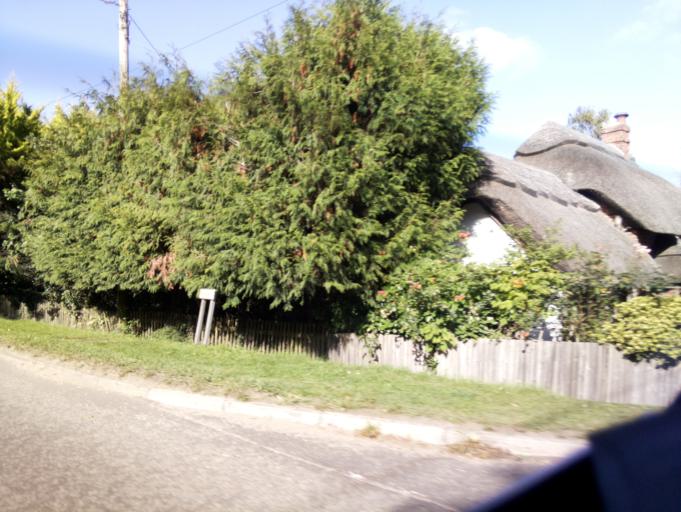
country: GB
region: England
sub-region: Hampshire
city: Tadley
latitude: 51.3403
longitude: -1.1281
